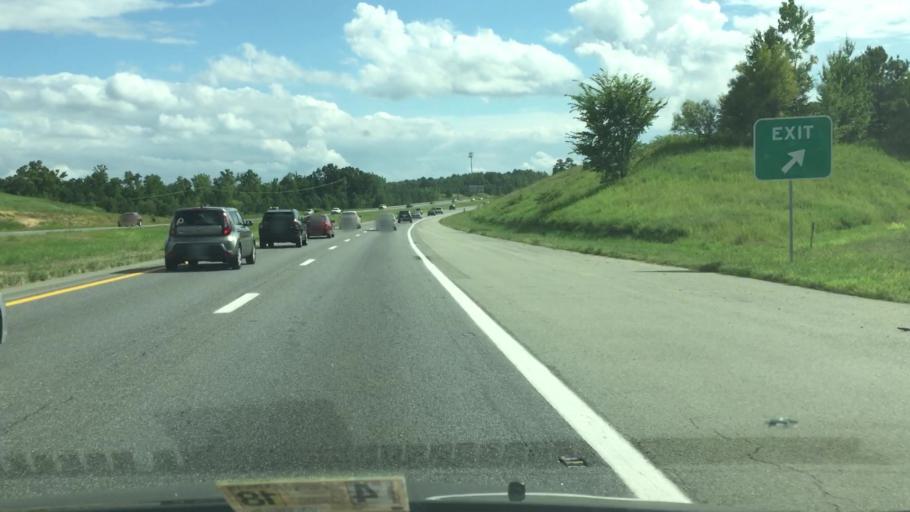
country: US
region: Virginia
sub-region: Henrico County
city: Short Pump
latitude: 37.5990
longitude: -77.6672
